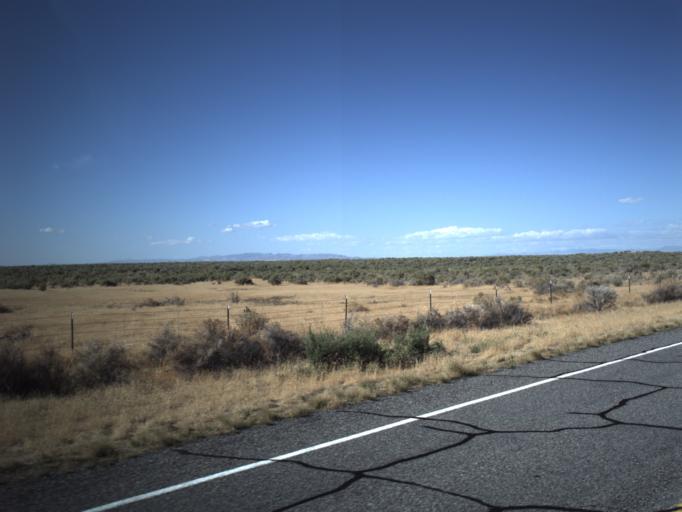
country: US
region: Utah
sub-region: Millard County
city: Delta
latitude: 39.3539
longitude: -112.4428
